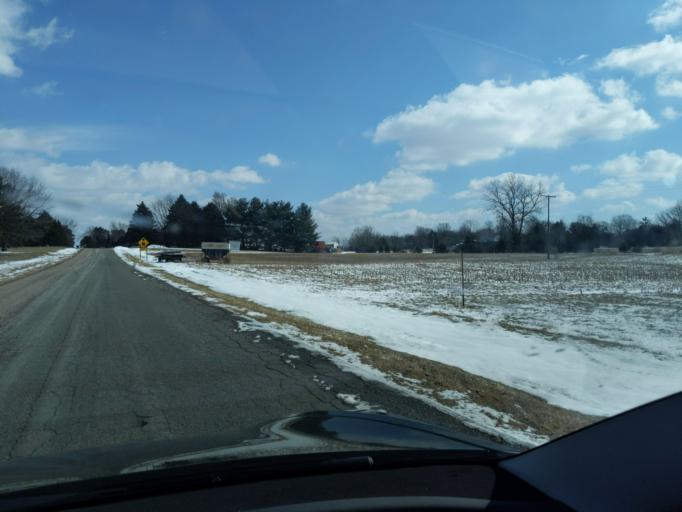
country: US
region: Michigan
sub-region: Ingham County
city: Williamston
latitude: 42.6154
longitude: -84.2634
